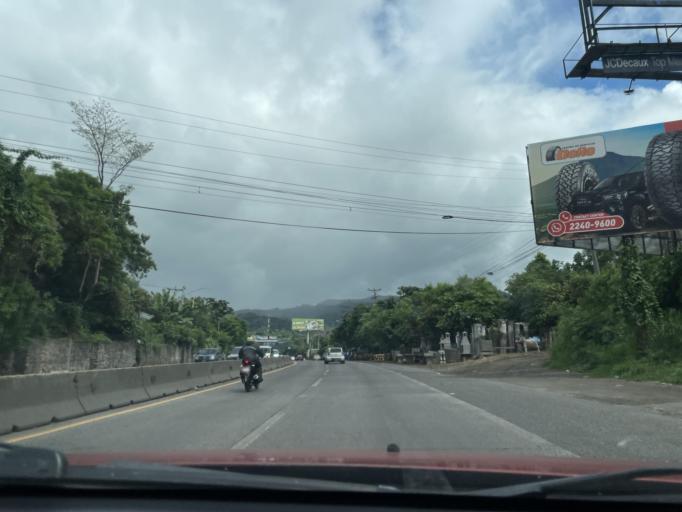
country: SV
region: La Libertad
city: Santa Tecla
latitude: 13.7167
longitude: -89.3552
